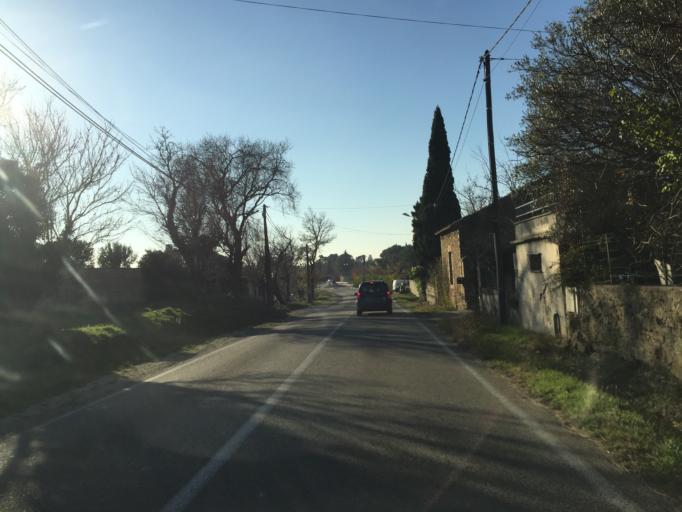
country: FR
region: Provence-Alpes-Cote d'Azur
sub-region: Departement du Vaucluse
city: Serignan-du-Comtat
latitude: 44.1906
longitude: 4.8548
